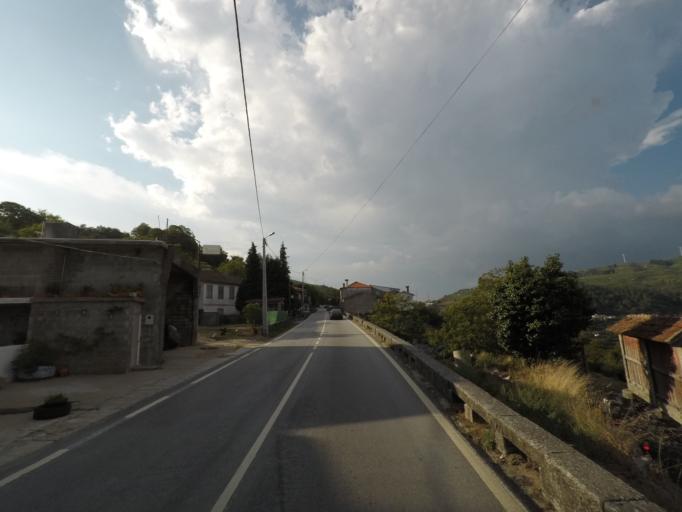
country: PT
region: Porto
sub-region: Baiao
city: Valadares
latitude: 41.1881
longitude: -7.9422
